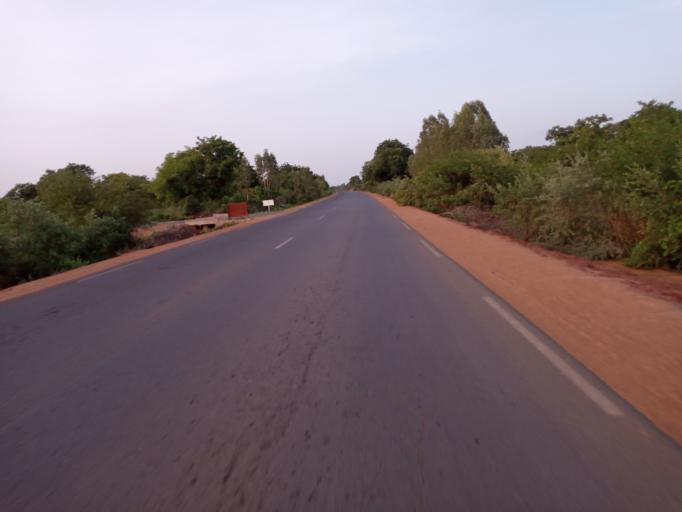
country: ML
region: Bamako
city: Bamako
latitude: 12.2886
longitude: -8.1715
